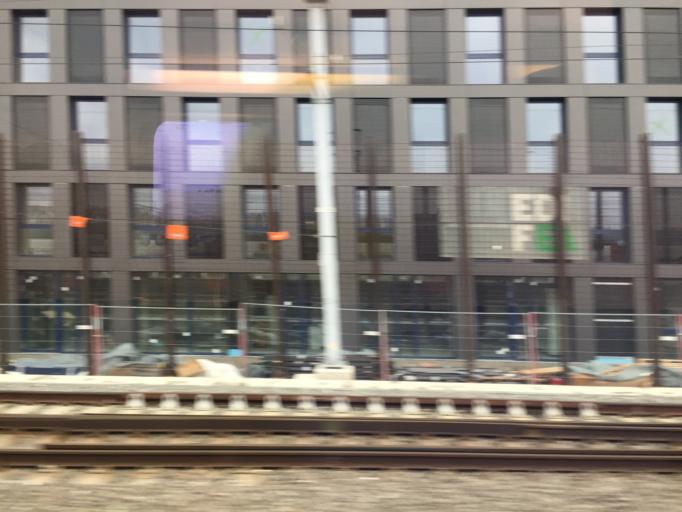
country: CH
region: Vaud
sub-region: Ouest Lausannois District
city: Renens
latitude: 46.5344
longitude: 6.5852
